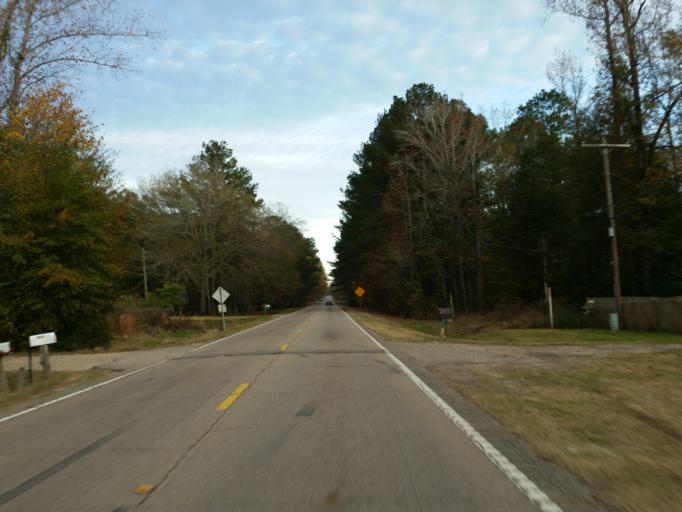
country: US
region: Mississippi
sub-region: Lauderdale County
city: Marion
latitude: 32.4191
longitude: -88.5200
